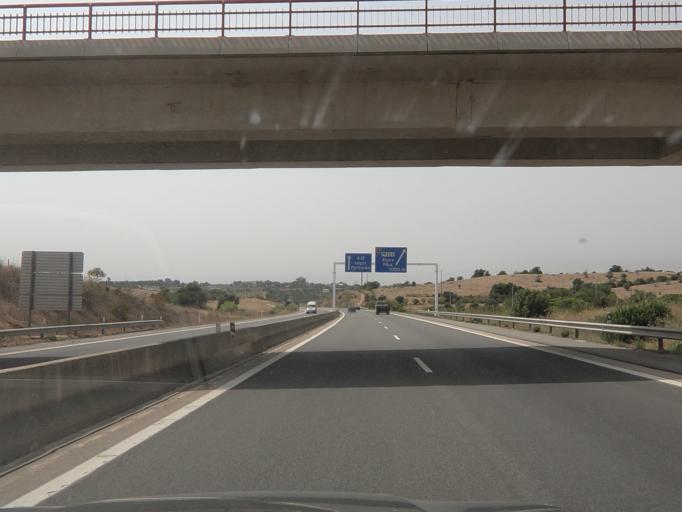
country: PT
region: Faro
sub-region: Albufeira
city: Guia
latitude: 37.1386
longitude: -8.3075
